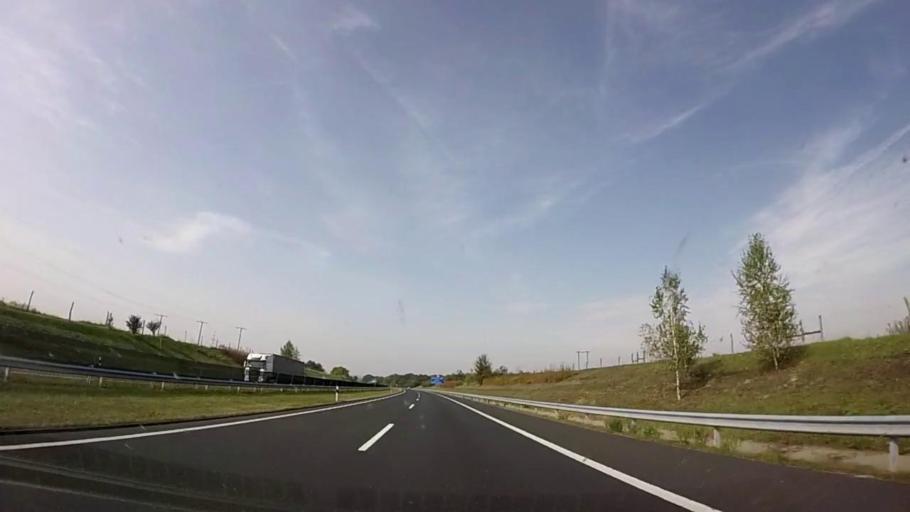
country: HU
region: Zala
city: Nagykanizsa
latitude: 46.4787
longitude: 16.9988
